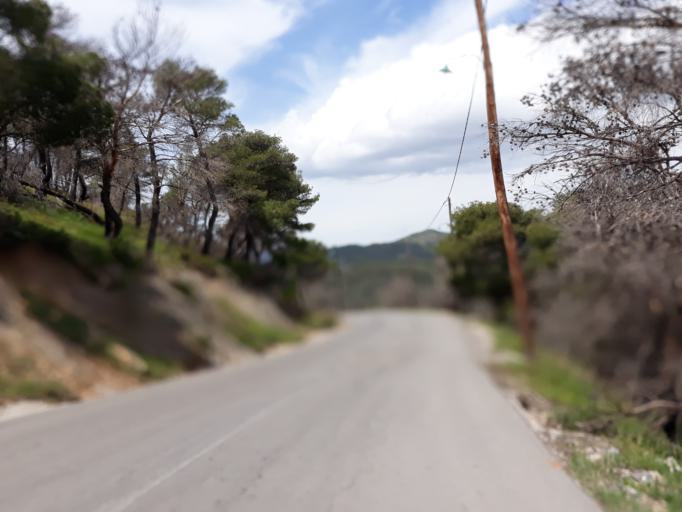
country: GR
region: Attica
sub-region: Nomarchia Dytikis Attikis
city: Magoula
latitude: 38.1595
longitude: 23.5334
